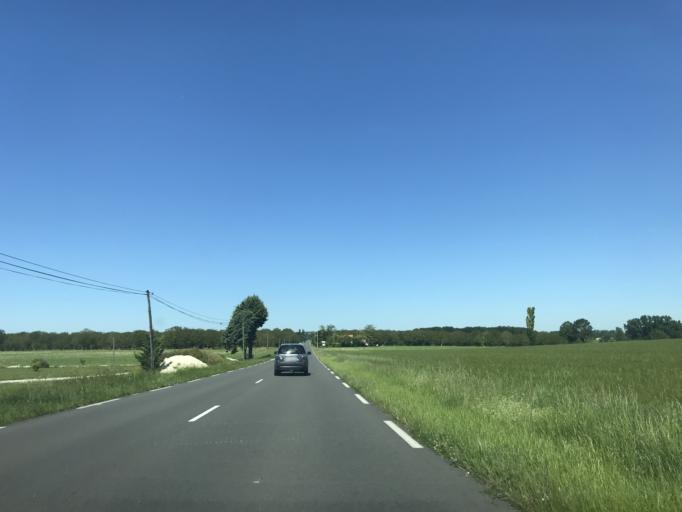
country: FR
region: Poitou-Charentes
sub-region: Departement de la Charente
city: Barbezieux-Saint-Hilaire
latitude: 45.4954
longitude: -0.2212
